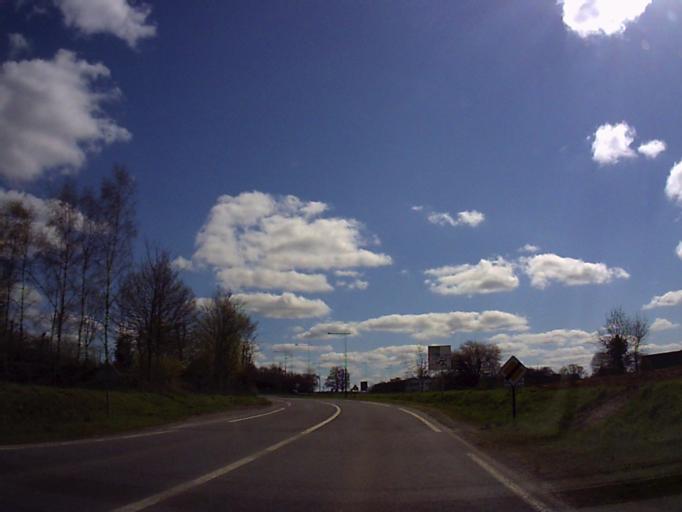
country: FR
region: Brittany
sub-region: Departement d'Ille-et-Vilaine
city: Saint-Meen-le-Grand
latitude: 48.1916
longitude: -2.1708
